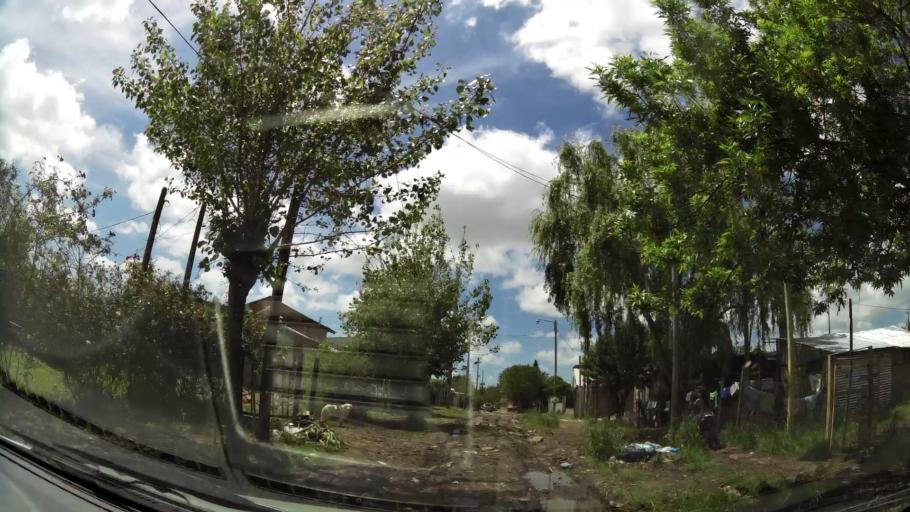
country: AR
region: Buenos Aires
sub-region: Partido de Quilmes
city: Quilmes
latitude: -34.8240
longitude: -58.2437
